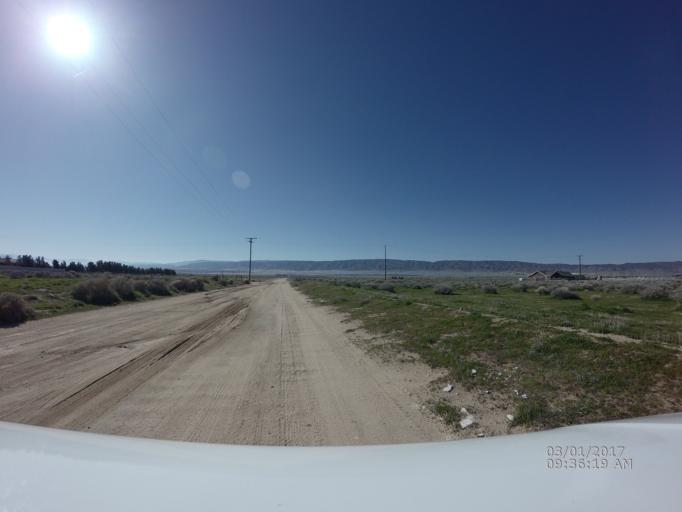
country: US
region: California
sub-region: Los Angeles County
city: Quartz Hill
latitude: 34.6971
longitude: -118.2718
